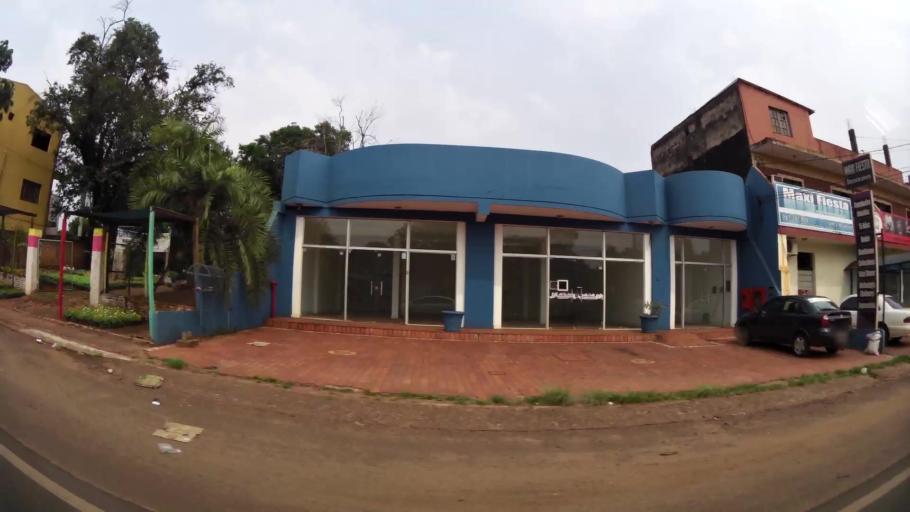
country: PY
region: Alto Parana
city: Presidente Franco
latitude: -25.5371
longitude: -54.6331
